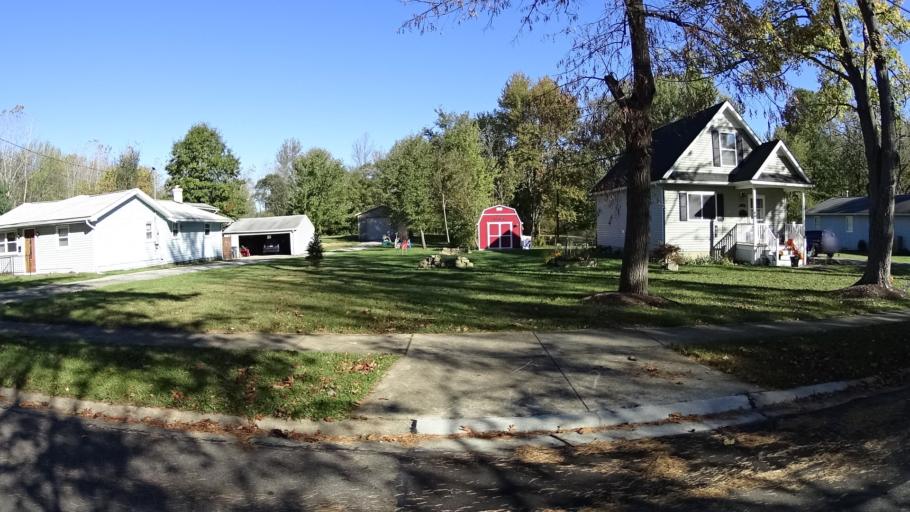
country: US
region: Ohio
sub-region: Lorain County
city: Oberlin
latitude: 41.2823
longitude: -82.2116
